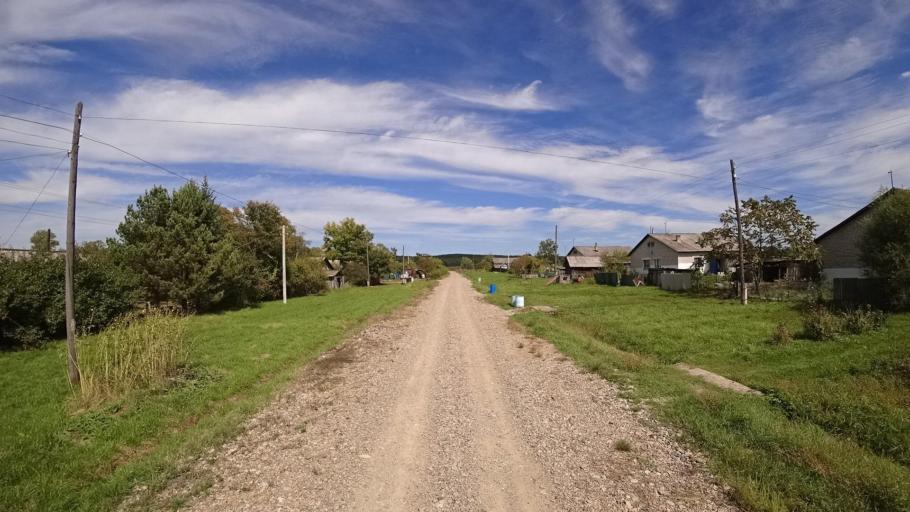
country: RU
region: Primorskiy
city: Yakovlevka
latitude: 44.6418
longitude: 133.6009
